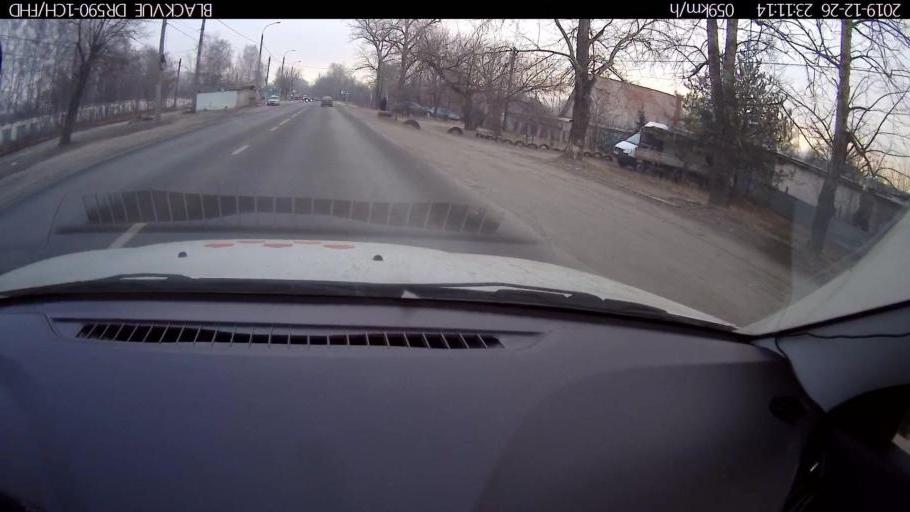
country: RU
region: Nizjnij Novgorod
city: Burevestnik
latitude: 56.2058
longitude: 43.7944
